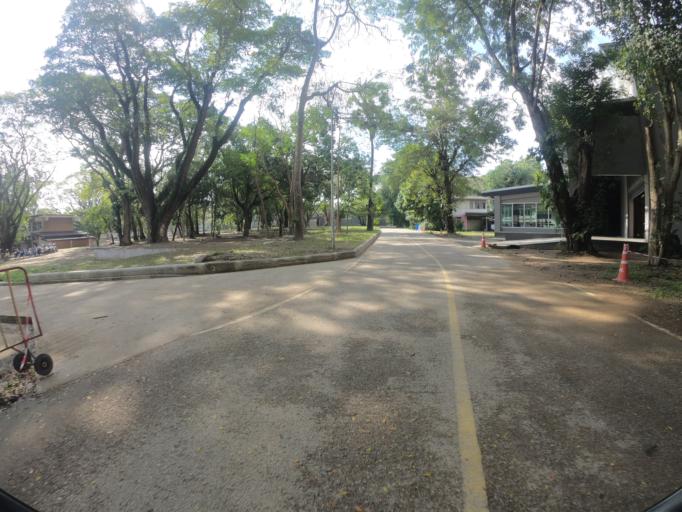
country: TH
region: Chiang Mai
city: Chiang Mai
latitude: 18.7954
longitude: 98.9503
